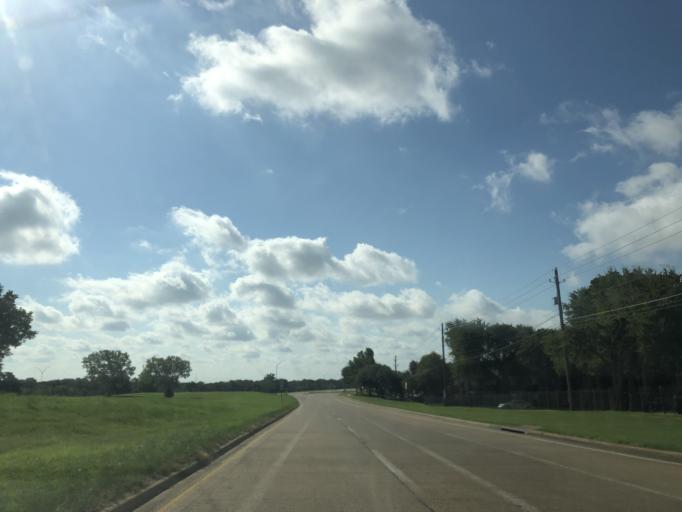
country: US
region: Texas
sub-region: Tarrant County
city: Euless
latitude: 32.8665
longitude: -97.0670
